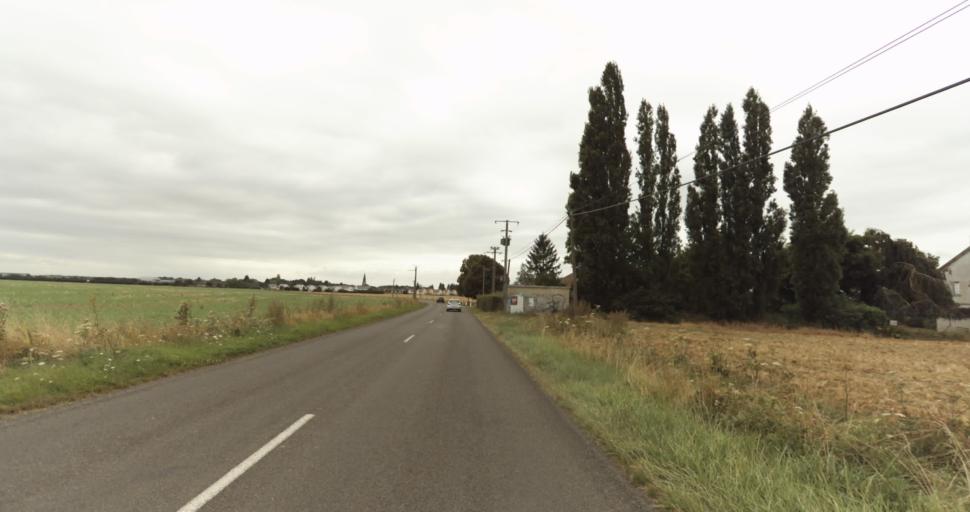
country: FR
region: Haute-Normandie
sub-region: Departement de l'Eure
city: Gravigny
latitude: 49.0440
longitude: 1.2129
